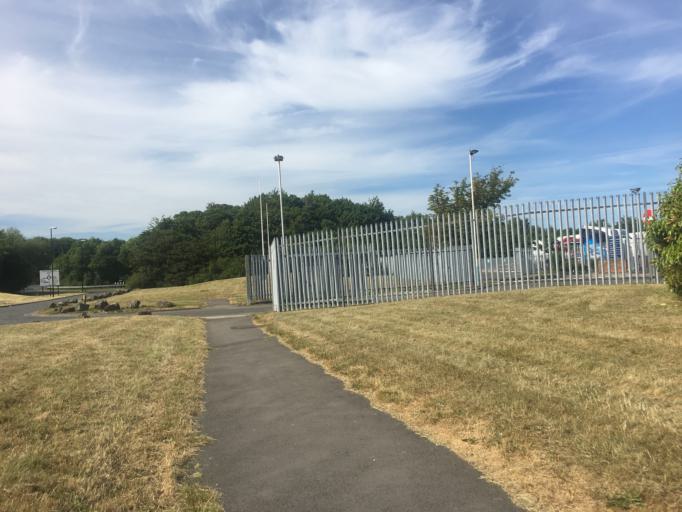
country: GB
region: England
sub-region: Sunderland
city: Washington
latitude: 54.8862
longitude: -1.5389
